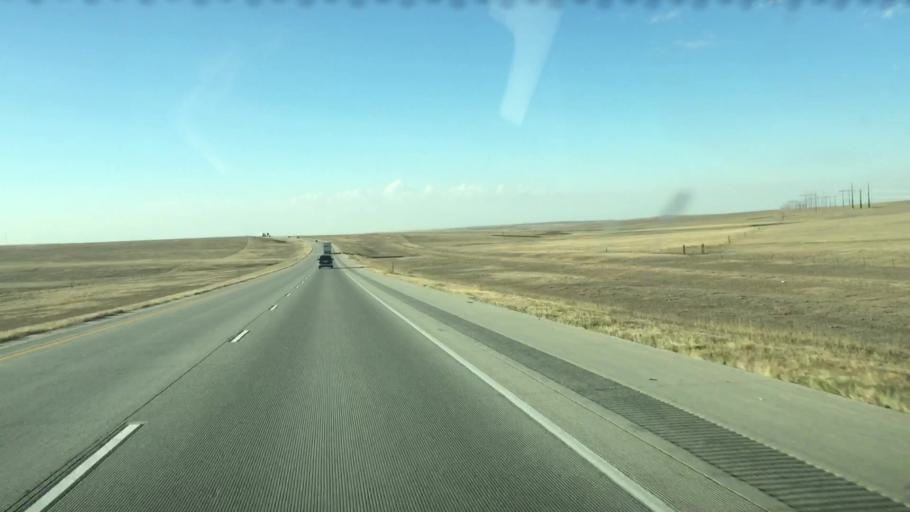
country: US
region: Colorado
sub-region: Lincoln County
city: Limon
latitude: 39.4083
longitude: -103.8985
